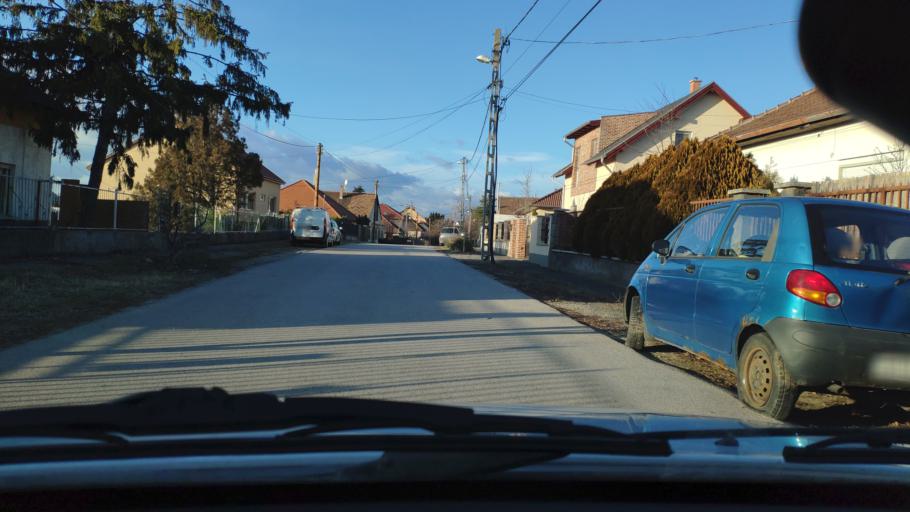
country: HU
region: Budapest
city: Budapest XXIII. keruelet
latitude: 47.3989
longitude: 19.0933
